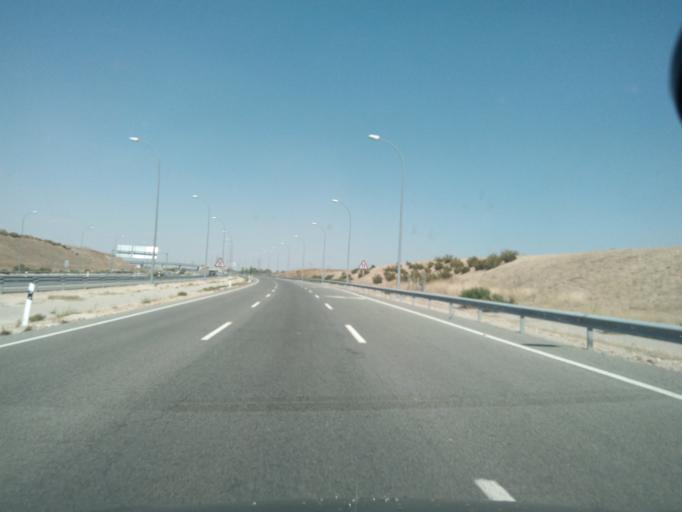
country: ES
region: Madrid
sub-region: Provincia de Madrid
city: Torrejon de Ardoz
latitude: 40.4675
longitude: -3.5047
